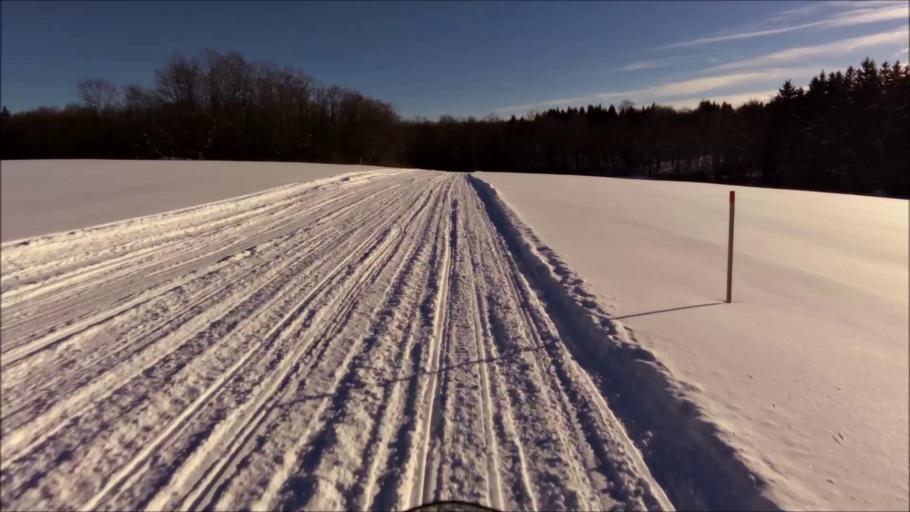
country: US
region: New York
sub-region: Chautauqua County
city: Mayville
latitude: 42.2509
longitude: -79.3859
